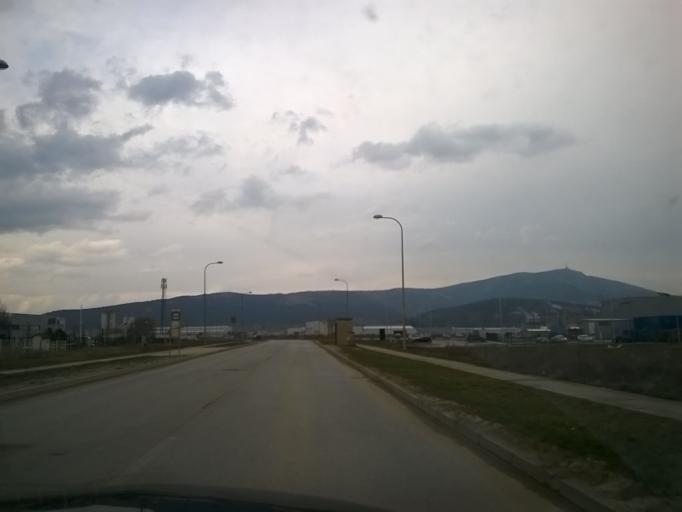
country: SK
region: Nitriansky
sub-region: Okres Nitra
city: Nitra
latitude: 48.3326
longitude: 18.0523
